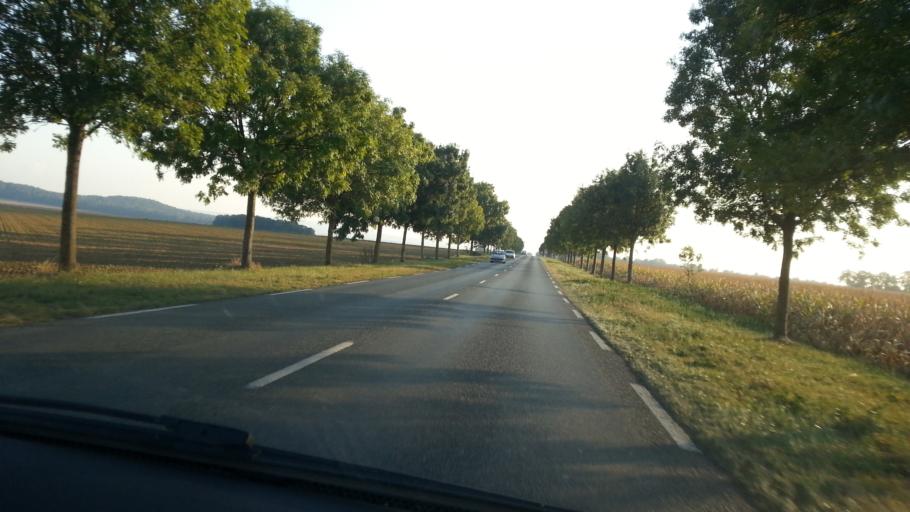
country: FR
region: Picardie
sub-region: Departement de l'Oise
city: Estrees-Saint-Denis
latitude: 49.3971
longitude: 2.6243
